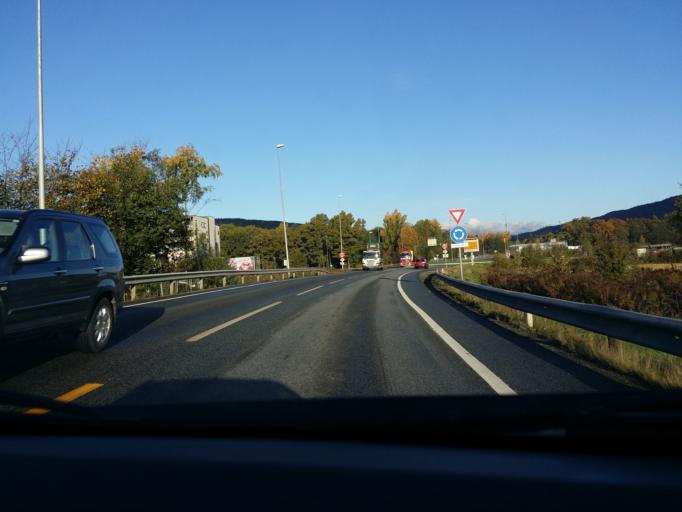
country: NO
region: Akershus
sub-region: Asker
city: Billingstad
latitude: 59.9085
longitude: 10.4809
